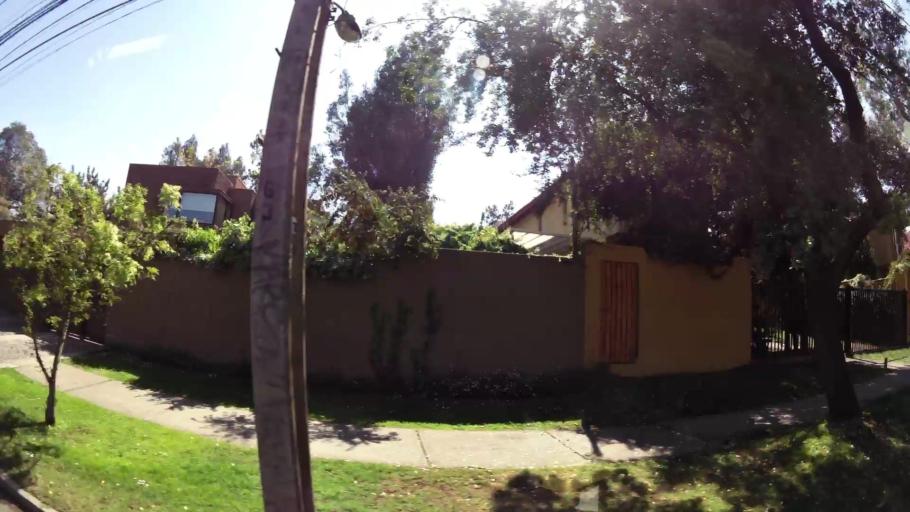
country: CL
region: Santiago Metropolitan
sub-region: Provincia de Santiago
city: Villa Presidente Frei, Nunoa, Santiago, Chile
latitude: -33.4411
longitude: -70.5313
